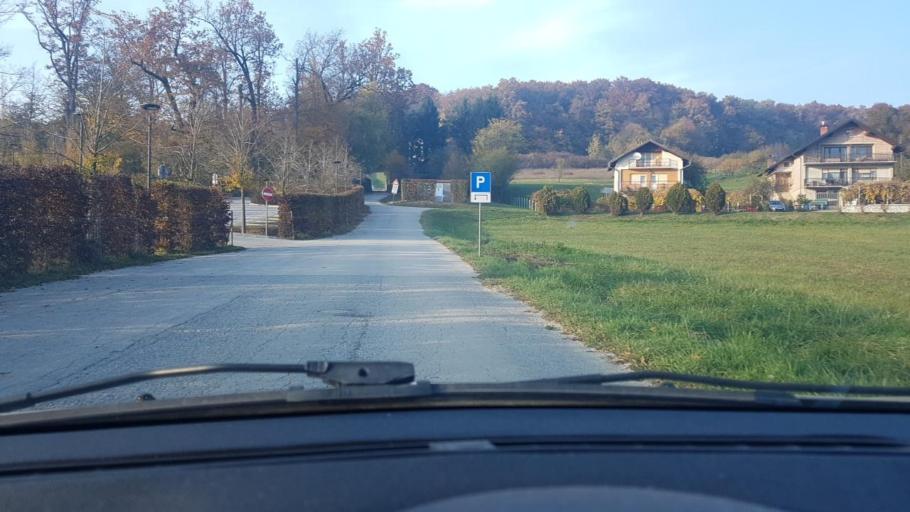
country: SI
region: Podcetrtek
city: Podcetrtek
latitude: 46.1286
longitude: 15.6170
